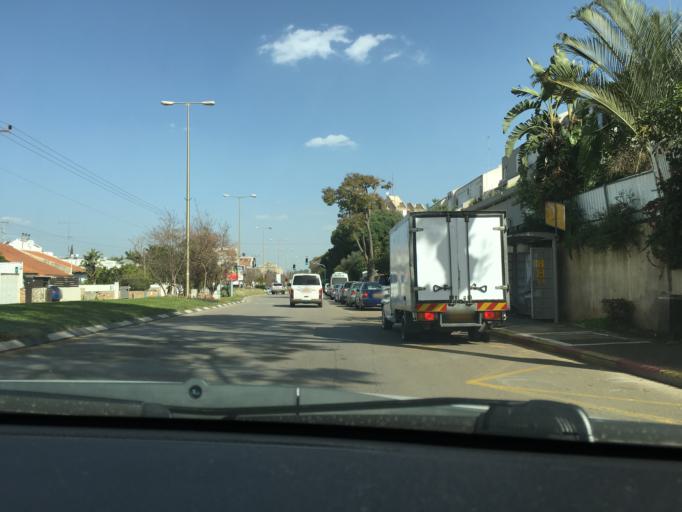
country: IL
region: Central District
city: Kfar Saba
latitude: 32.1834
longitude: 34.9004
